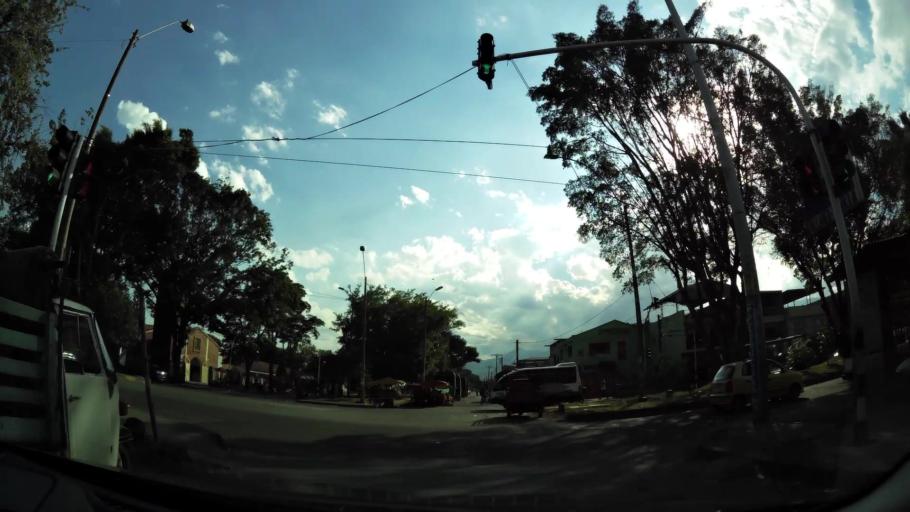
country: CO
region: Valle del Cauca
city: Cali
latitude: 3.4062
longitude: -76.5147
